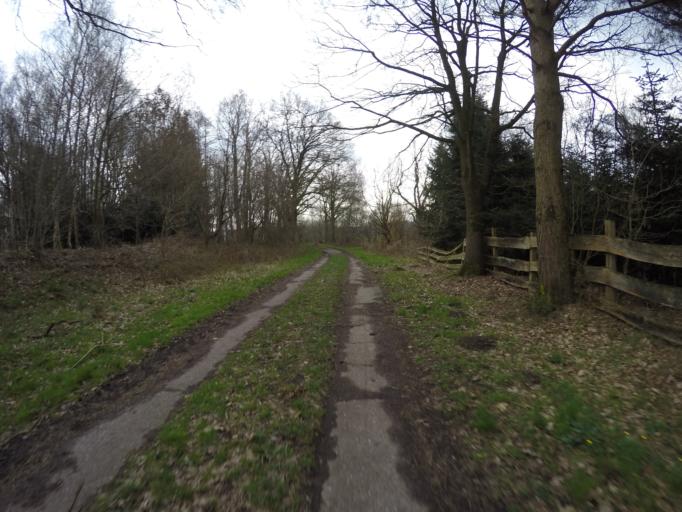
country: DE
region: Schleswig-Holstein
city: Ellerhoop
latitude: 53.7283
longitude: 9.8076
